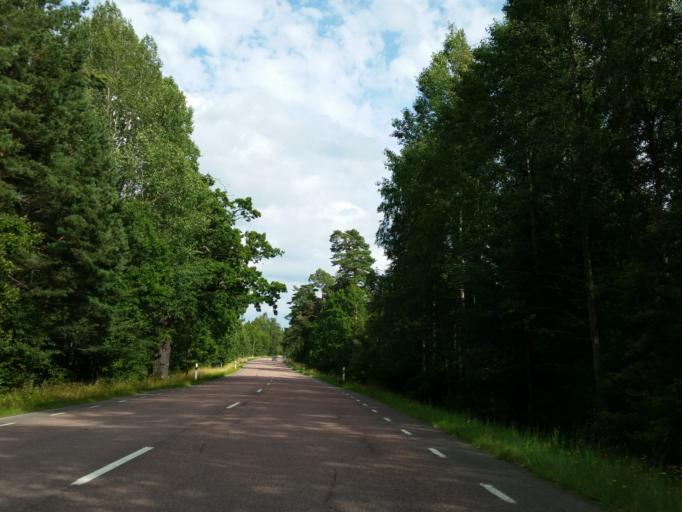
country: SE
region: Soedermanland
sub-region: Strangnas Kommun
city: Mariefred
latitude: 59.2217
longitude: 17.2704
